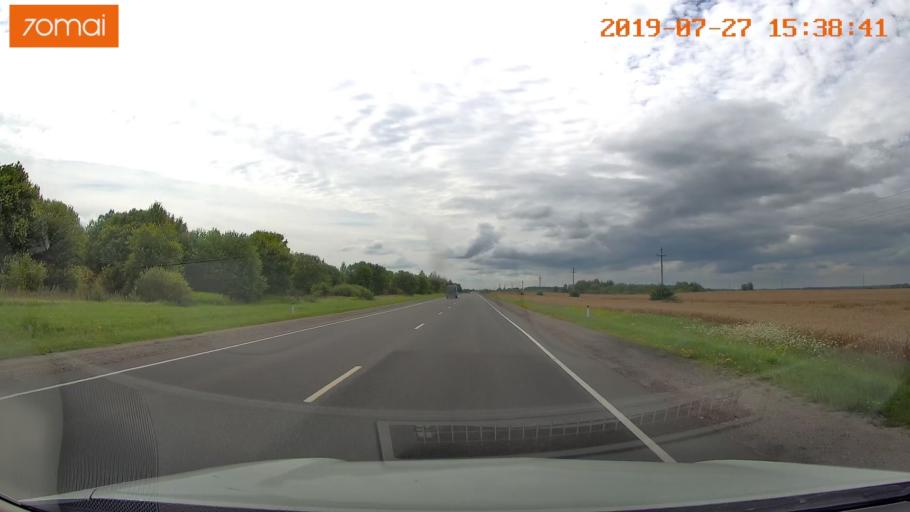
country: RU
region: Kaliningrad
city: Gusev
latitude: 54.6073
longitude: 22.3079
